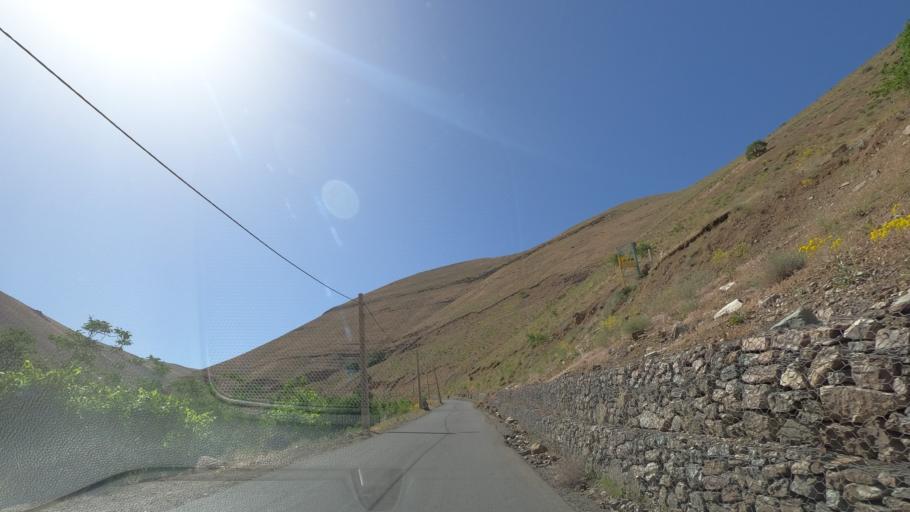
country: IR
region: Alborz
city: Karaj
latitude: 35.9418
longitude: 51.0836
